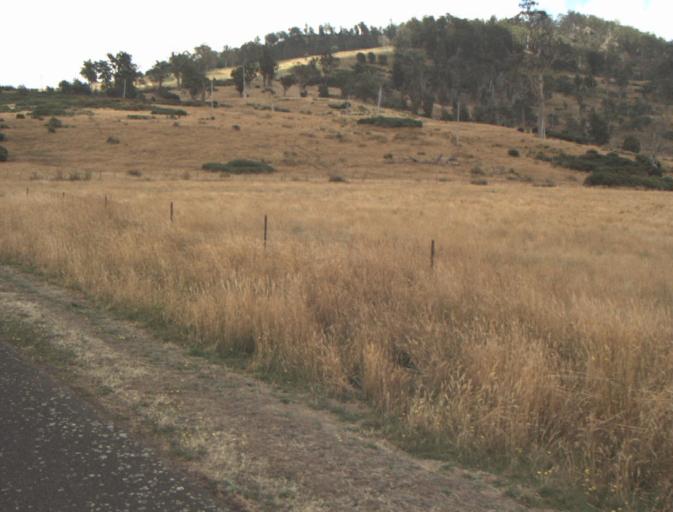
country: AU
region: Tasmania
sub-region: Northern Midlands
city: Evandale
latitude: -41.5094
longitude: 147.4795
